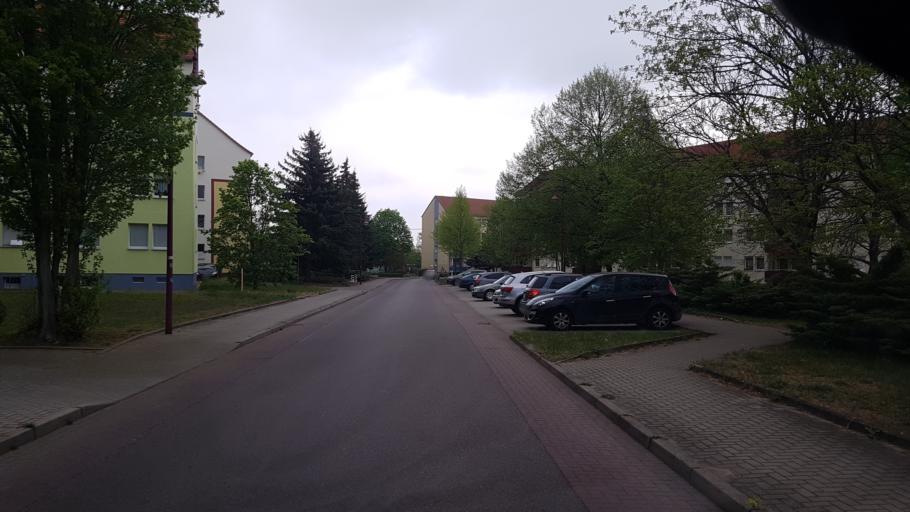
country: DE
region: Brandenburg
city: Grossraschen
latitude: 51.5890
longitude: 13.9971
